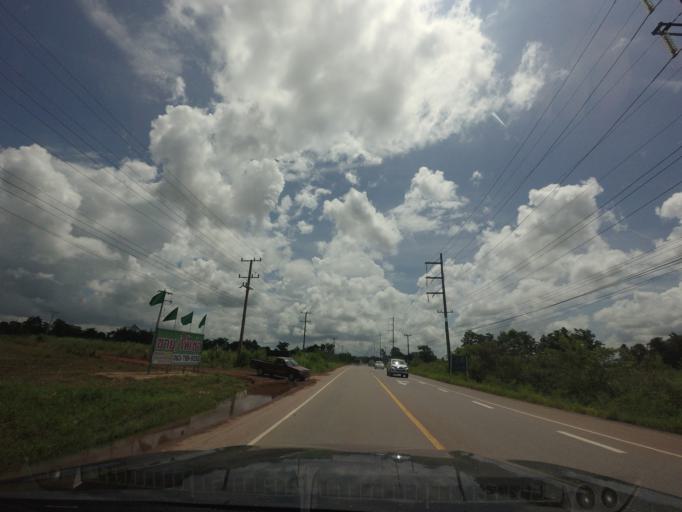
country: TH
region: Changwat Udon Thani
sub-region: Amphoe Ban Phue
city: Ban Phue
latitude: 17.6649
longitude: 102.5101
